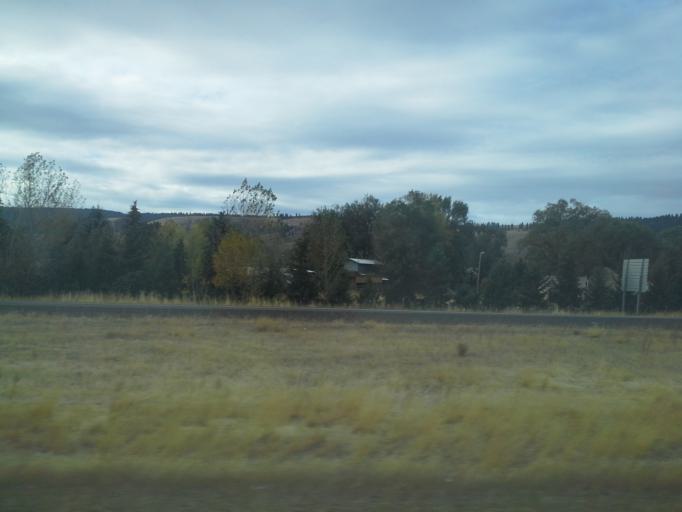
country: US
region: Oregon
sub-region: Union County
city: La Grande
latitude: 45.3373
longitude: -118.0779
